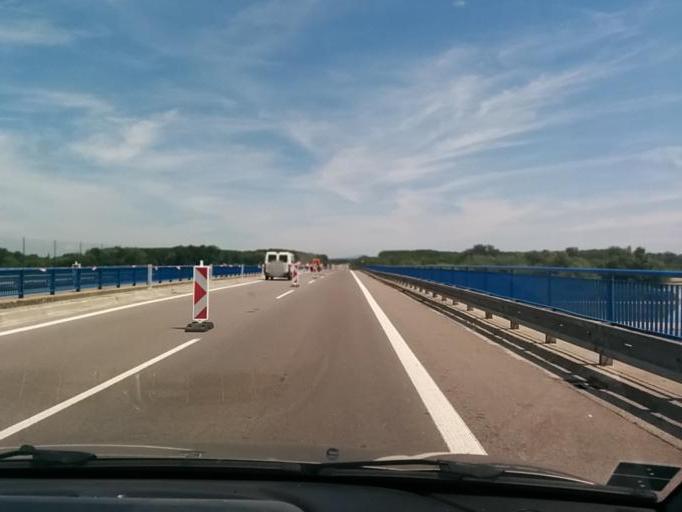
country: SK
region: Trnavsky
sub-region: Okres Galanta
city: Galanta
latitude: 48.2582
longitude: 17.7791
